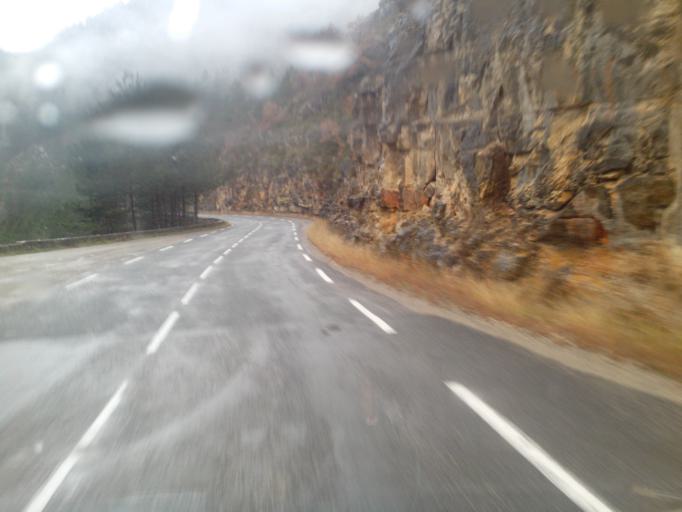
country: FR
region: Languedoc-Roussillon
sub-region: Departement de la Lozere
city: Chanac
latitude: 44.3596
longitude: 3.4456
